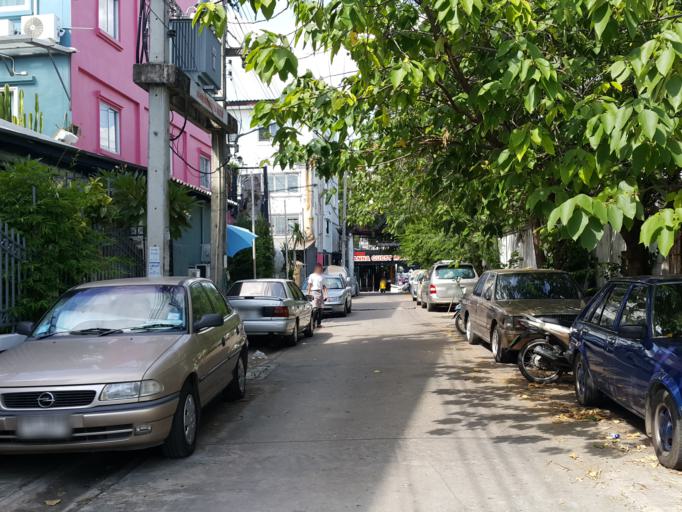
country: TH
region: Chiang Mai
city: Chiang Mai
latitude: 18.7878
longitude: 98.9833
